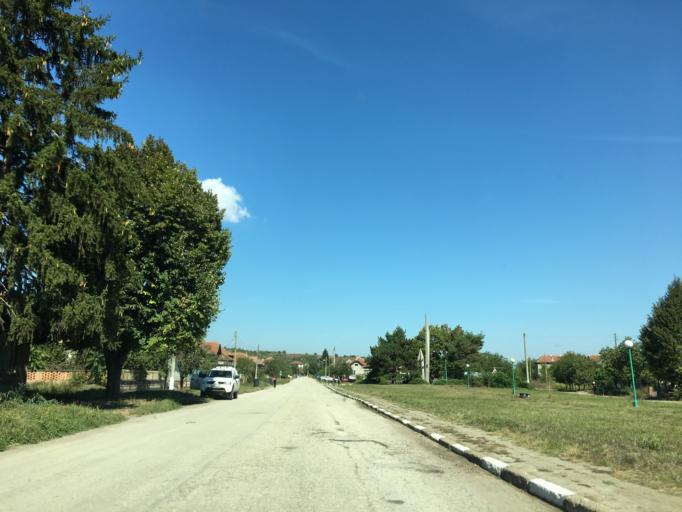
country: RO
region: Olt
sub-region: Comuna Orlea
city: Orlea
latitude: 43.6407
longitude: 24.3988
